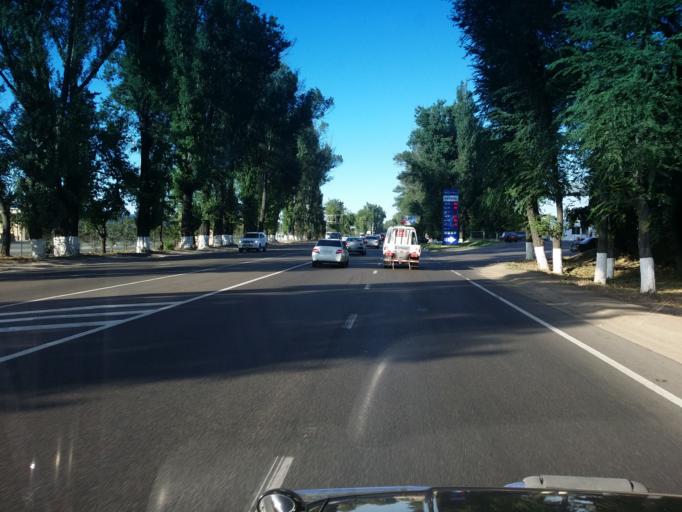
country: KZ
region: Almaty Qalasy
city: Almaty
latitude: 43.2989
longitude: 77.0027
